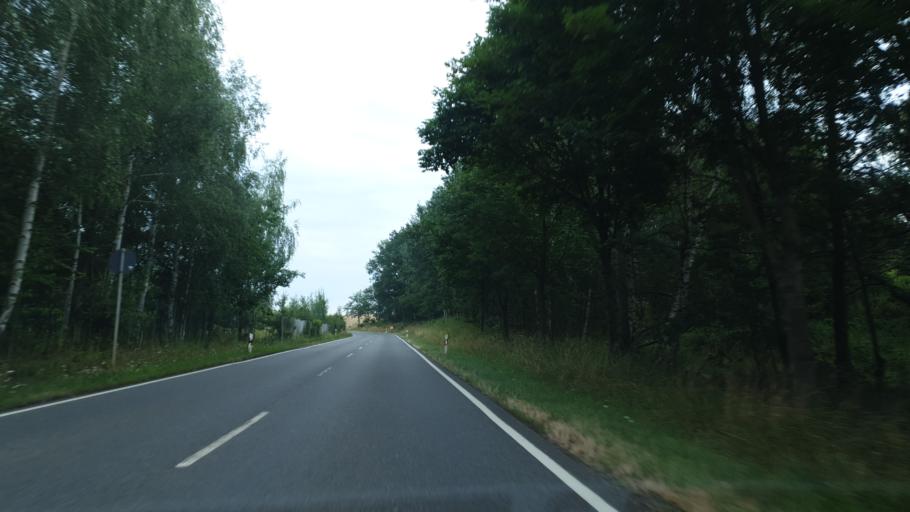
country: DE
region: Saxony
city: Sankt Egidien
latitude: 50.7974
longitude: 12.6152
